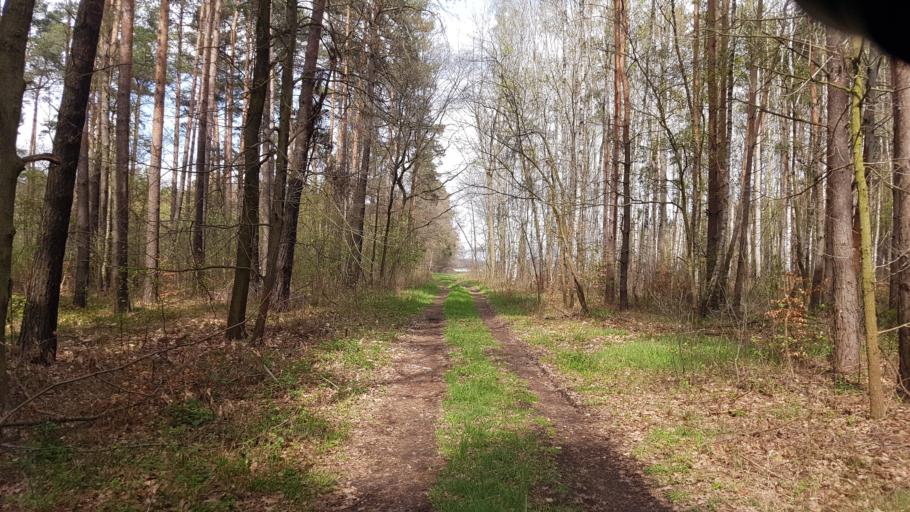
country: DE
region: Brandenburg
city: Bronkow
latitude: 51.6105
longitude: 13.9310
